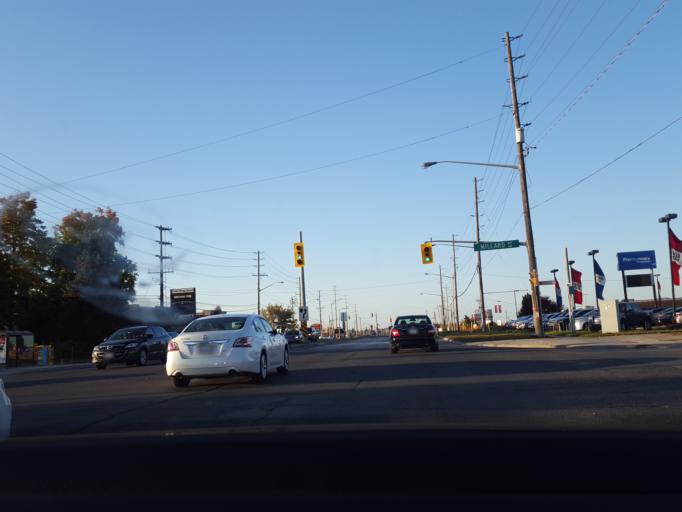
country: CA
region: Ontario
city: Newmarket
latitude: 44.0508
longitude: -79.4793
